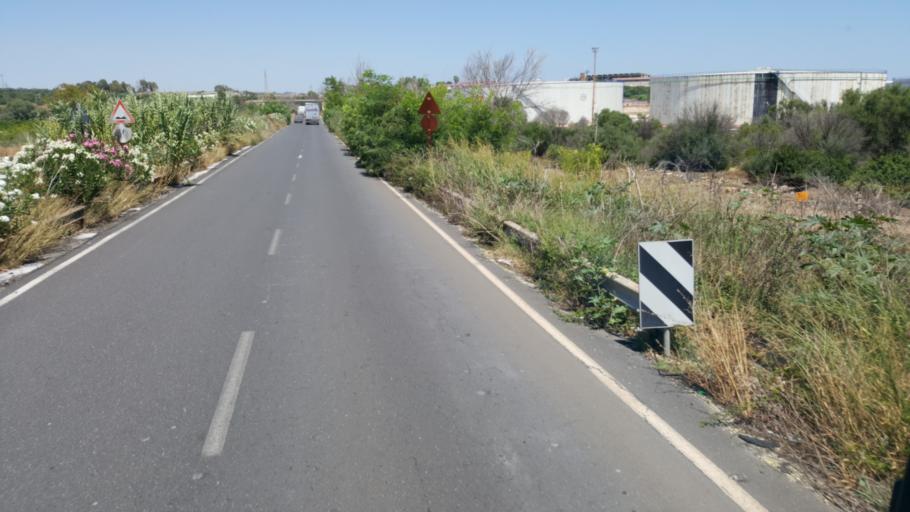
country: IT
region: Sicily
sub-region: Provincia di Siracusa
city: Melilli
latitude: 37.2083
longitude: 15.1578
